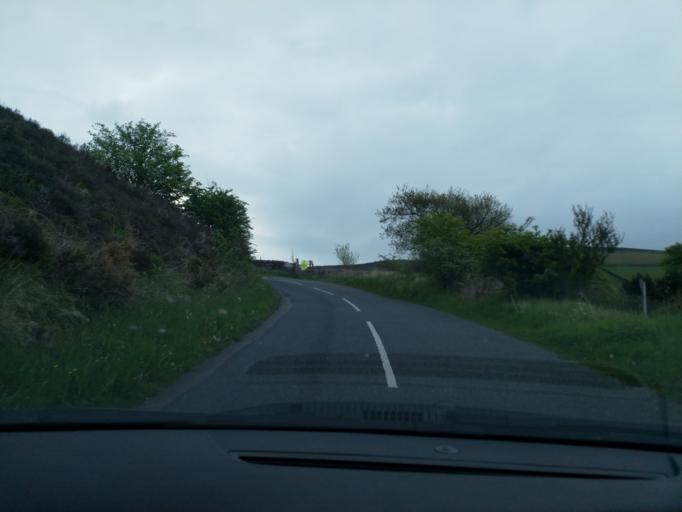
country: GB
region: England
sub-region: Derbyshire
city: Hathersage
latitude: 53.3328
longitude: -1.6314
